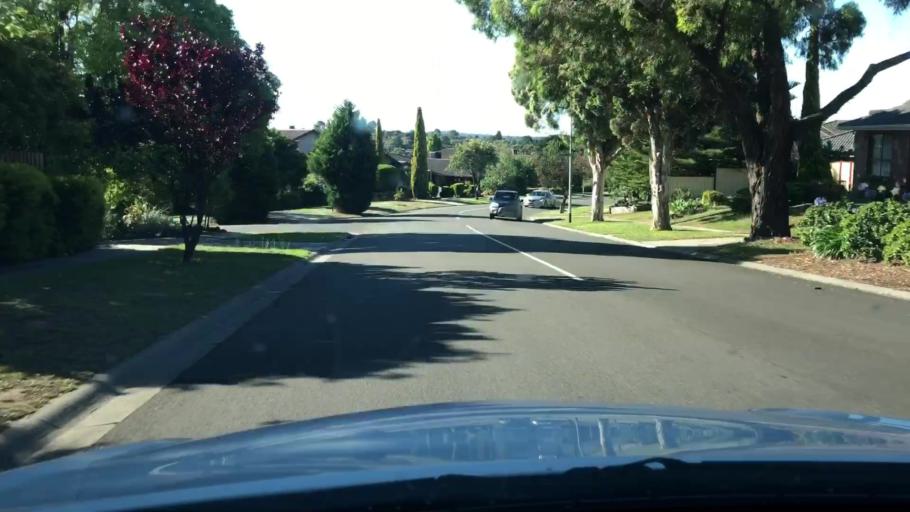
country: AU
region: Victoria
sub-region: Casey
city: Endeavour Hills
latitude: -37.9779
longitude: 145.2497
